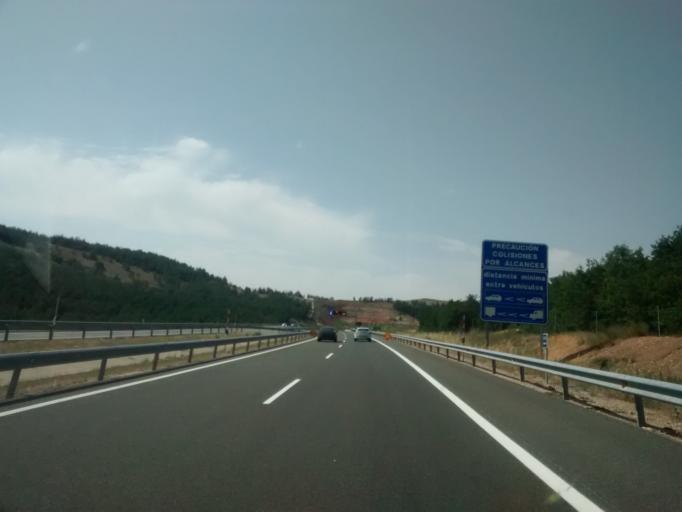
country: ES
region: Castille and Leon
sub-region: Provincia de Palencia
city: Alar del Rey
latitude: 42.6926
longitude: -4.2988
